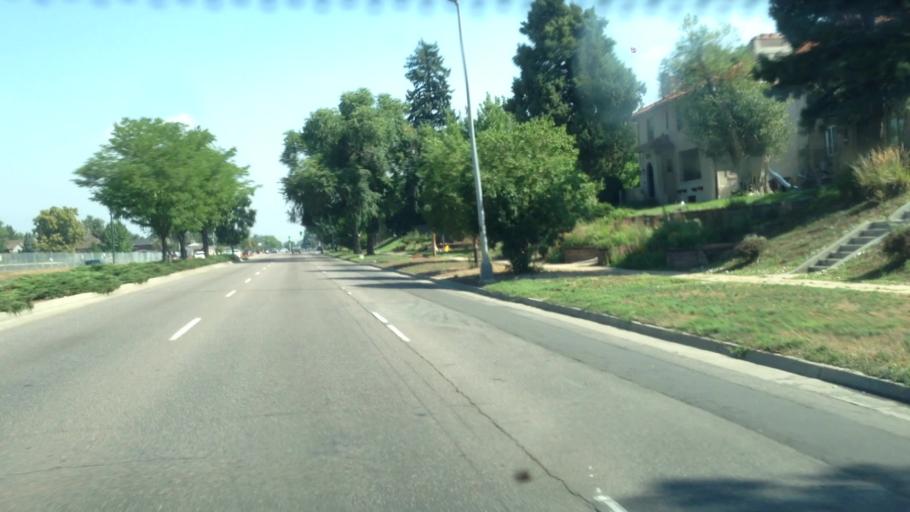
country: US
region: Colorado
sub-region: Denver County
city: Denver
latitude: 39.7522
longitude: -104.9406
